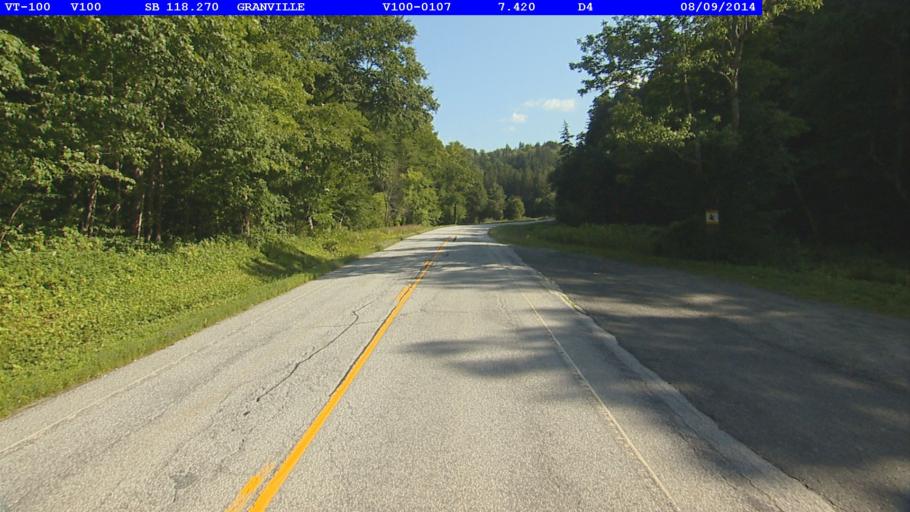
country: US
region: Vermont
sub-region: Orange County
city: Randolph
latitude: 44.0370
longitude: -72.8318
